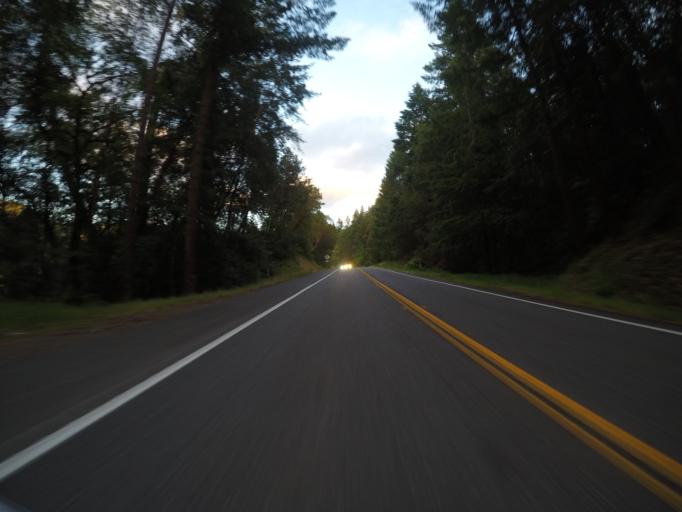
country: US
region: California
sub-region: Humboldt County
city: Redway
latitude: 40.0069
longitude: -123.7884
